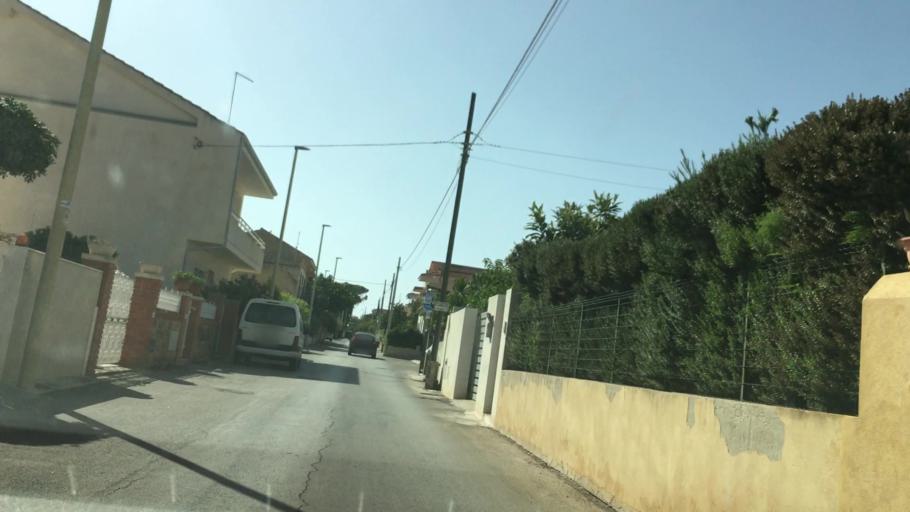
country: IT
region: Sicily
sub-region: Ragusa
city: Pozzallo
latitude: 36.7146
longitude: 14.7778
